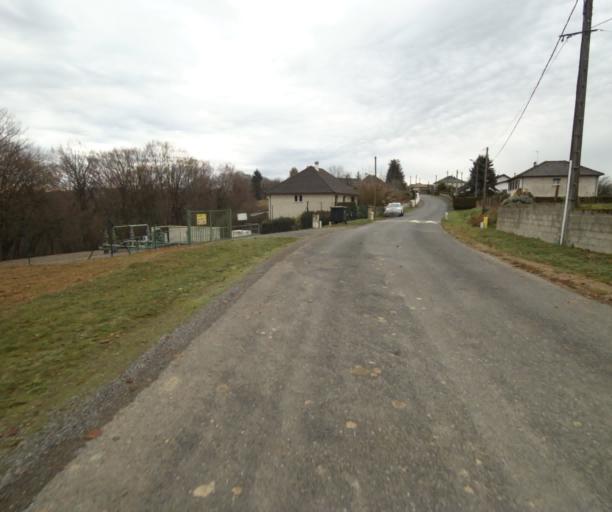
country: FR
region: Limousin
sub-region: Departement de la Correze
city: Tulle
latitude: 45.2509
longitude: 1.7341
